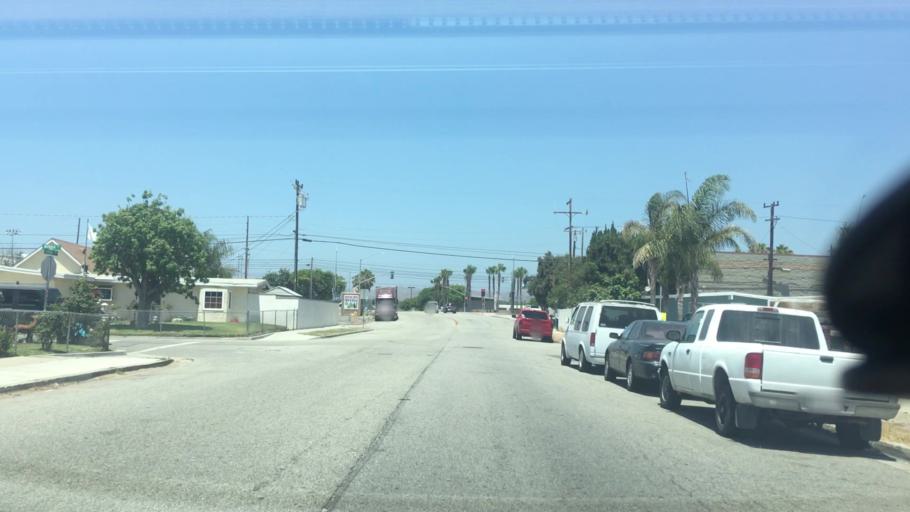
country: US
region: California
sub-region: Ventura County
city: El Rio
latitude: 34.2431
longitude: -119.1625
